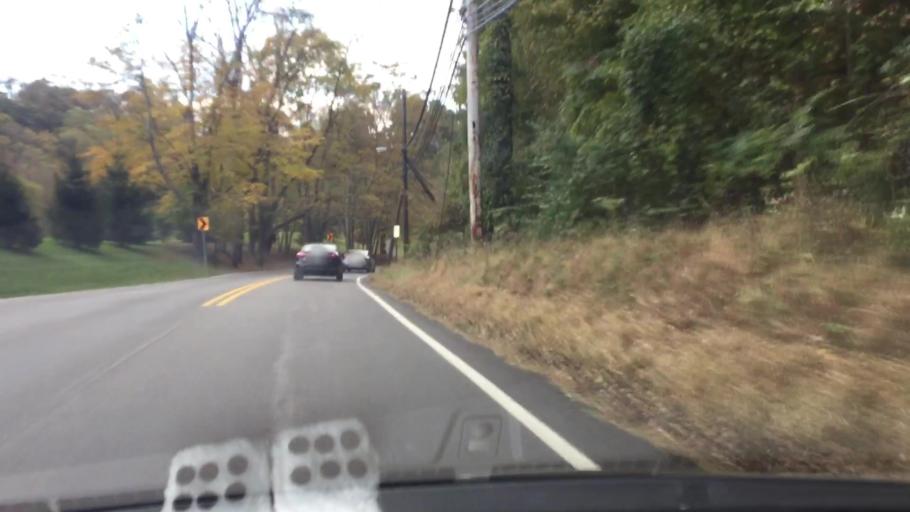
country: US
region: Pennsylvania
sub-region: Delaware County
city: Media
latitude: 39.9212
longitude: -75.4050
